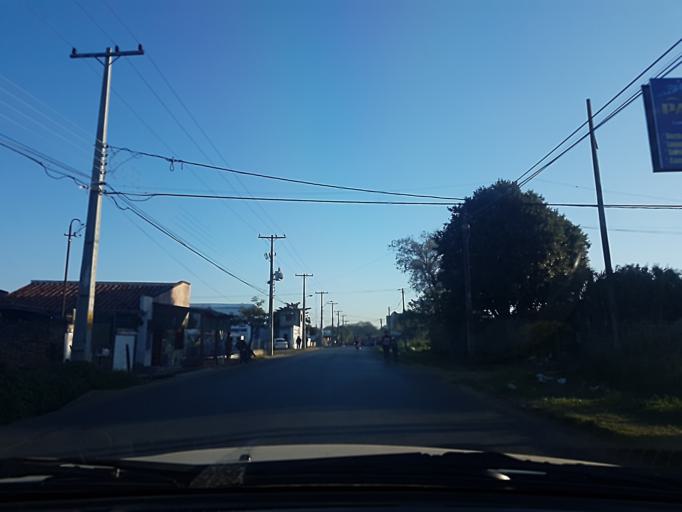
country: PY
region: Central
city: Colonia Mariano Roque Alonso
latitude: -25.2192
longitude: -57.5211
